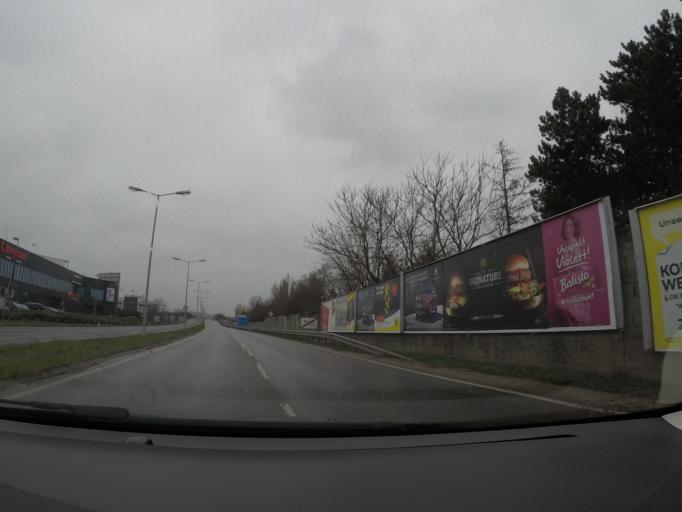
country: AT
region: Lower Austria
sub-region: Politischer Bezirk Modling
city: Brunn am Gebirge
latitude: 48.1132
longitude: 16.3037
